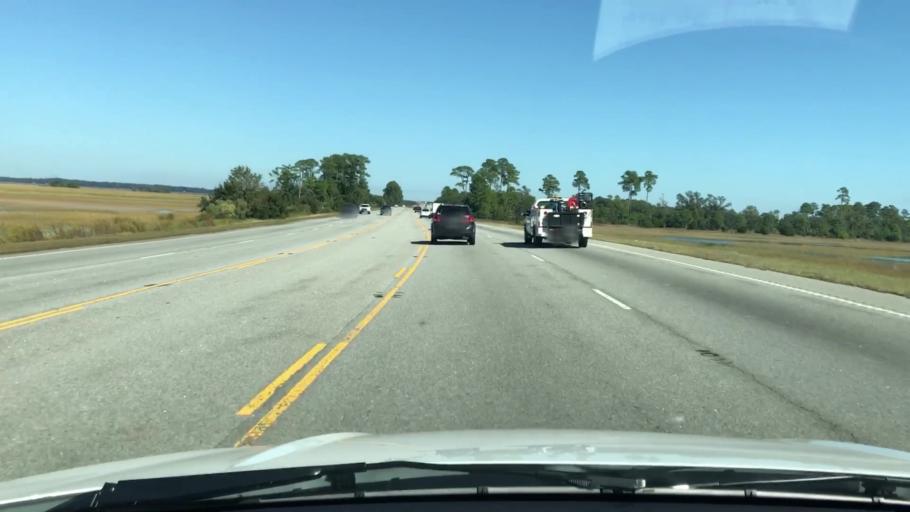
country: US
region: South Carolina
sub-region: Beaufort County
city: Shell Point
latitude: 32.3708
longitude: -80.8047
